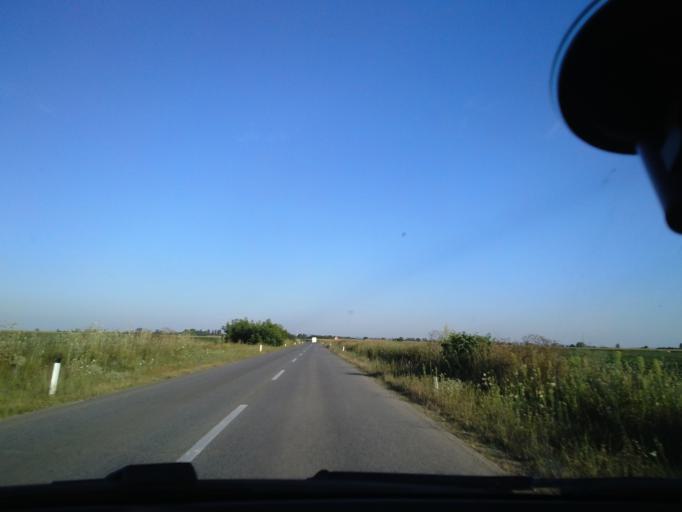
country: RS
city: Obrovac
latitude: 45.4276
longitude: 19.3858
